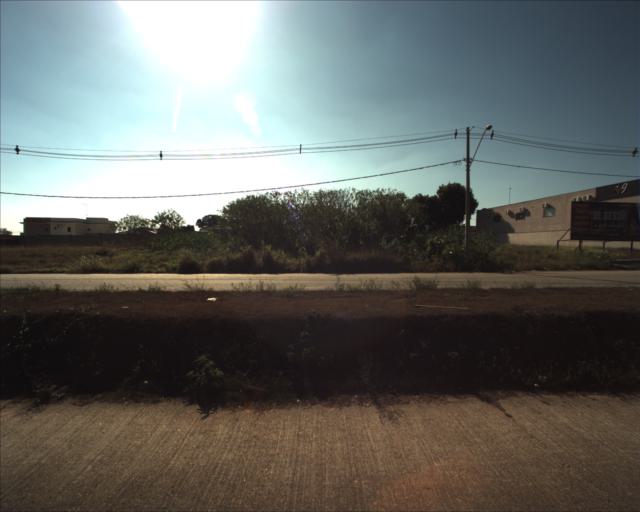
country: BR
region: Sao Paulo
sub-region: Sorocaba
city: Sorocaba
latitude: -23.4152
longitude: -47.4010
